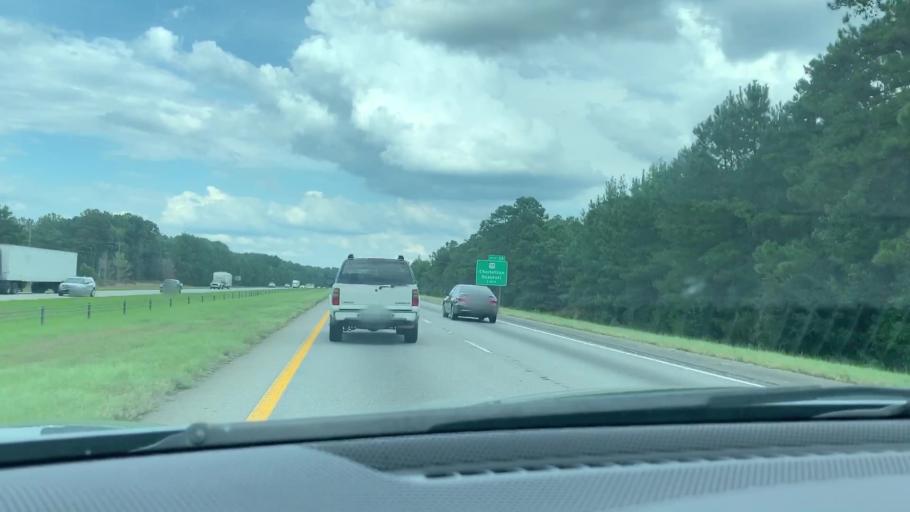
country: US
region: South Carolina
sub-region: Hampton County
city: Yemassee
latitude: 32.6136
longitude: -80.8937
